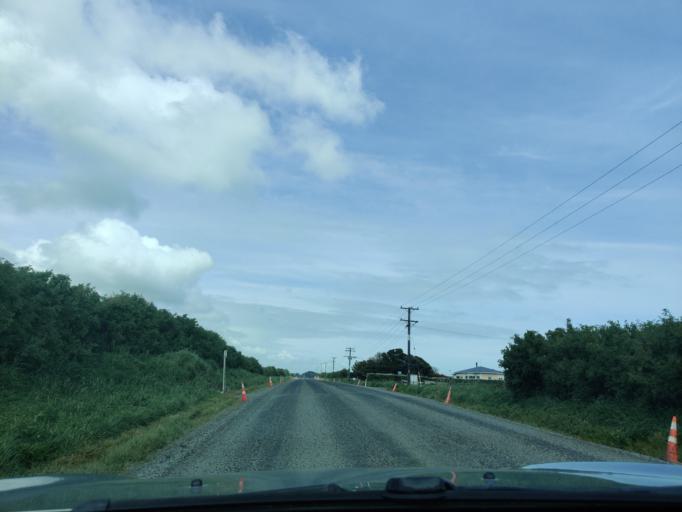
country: NZ
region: Taranaki
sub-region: South Taranaki District
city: Hawera
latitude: -39.5827
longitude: 174.2361
